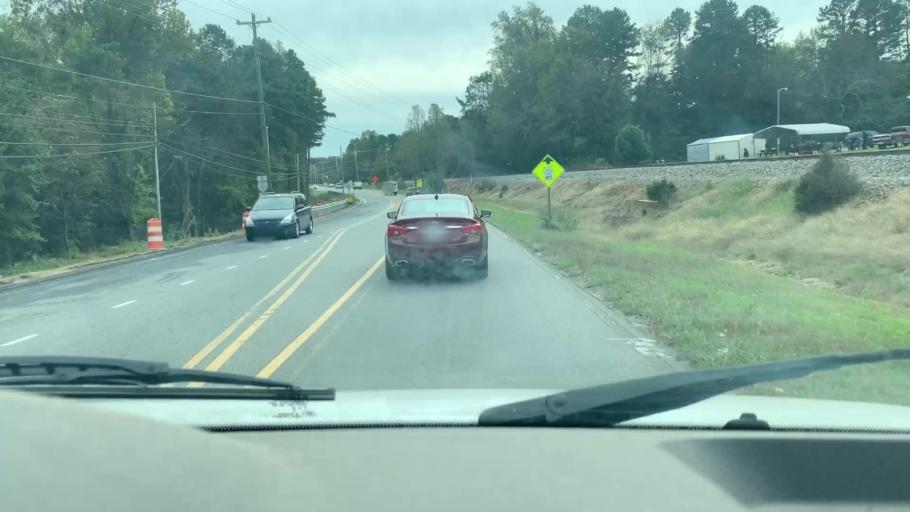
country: US
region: North Carolina
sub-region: Gaston County
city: Davidson
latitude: 35.5386
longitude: -80.8479
